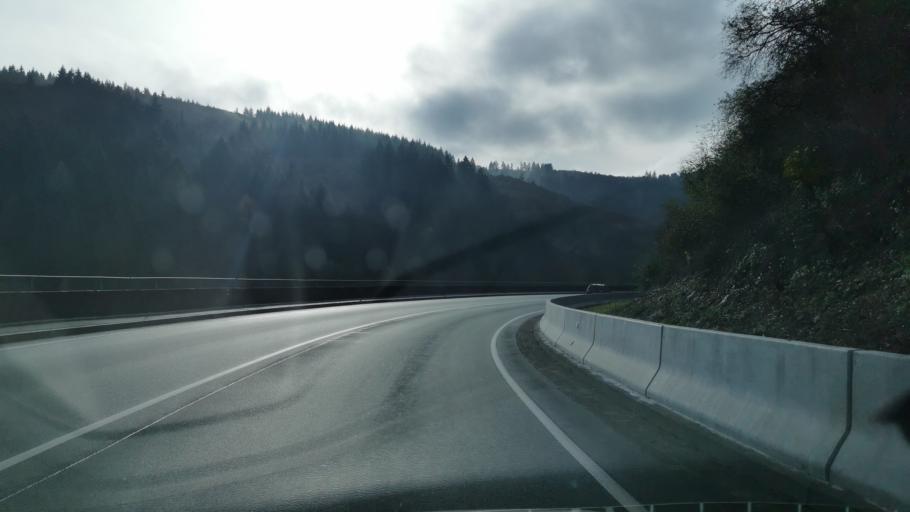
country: DE
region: Rheinland-Pfalz
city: Cochem
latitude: 50.1348
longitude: 7.1734
